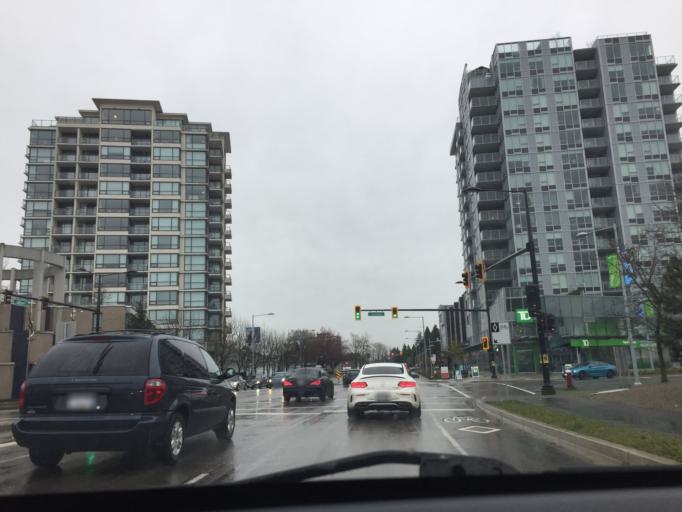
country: CA
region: British Columbia
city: Richmond
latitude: 49.1743
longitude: -123.1454
